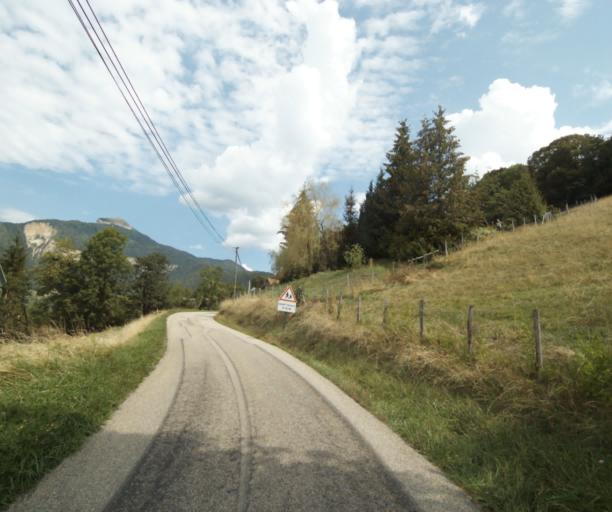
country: FR
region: Rhone-Alpes
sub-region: Departement de l'Isere
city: Le Sappey-en-Chartreuse
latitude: 45.2538
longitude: 5.7423
